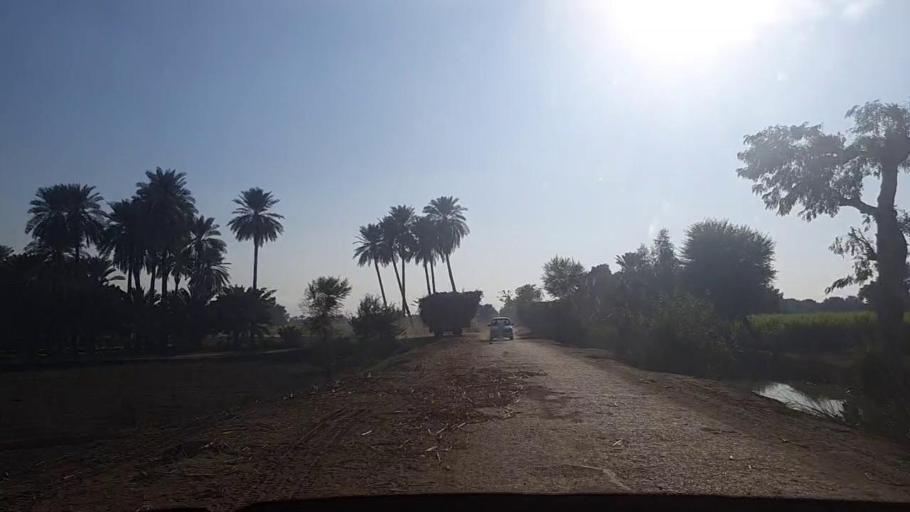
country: PK
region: Sindh
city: Gambat
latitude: 27.3545
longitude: 68.4538
